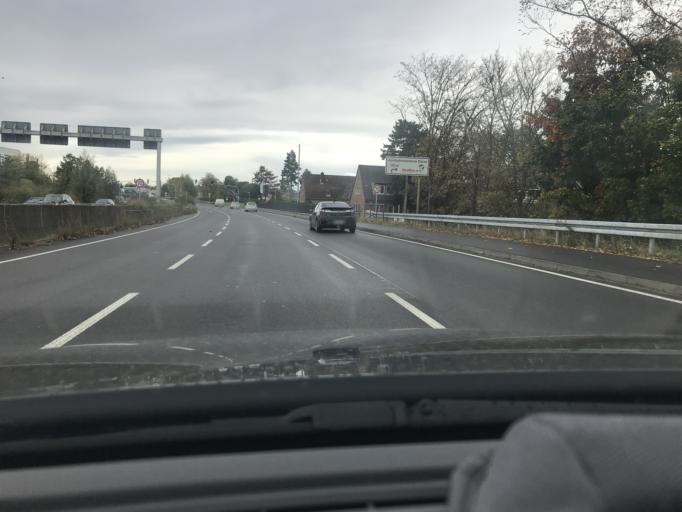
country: DE
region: North Rhine-Westphalia
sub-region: Regierungsbezirk Koln
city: Niederzier
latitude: 50.8374
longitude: 6.4536
